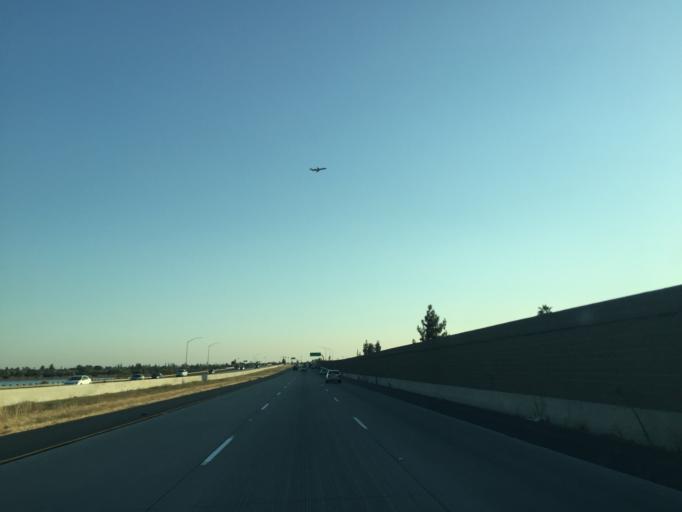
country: US
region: California
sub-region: Fresno County
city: Tarpey Village
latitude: 36.8002
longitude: -119.7416
